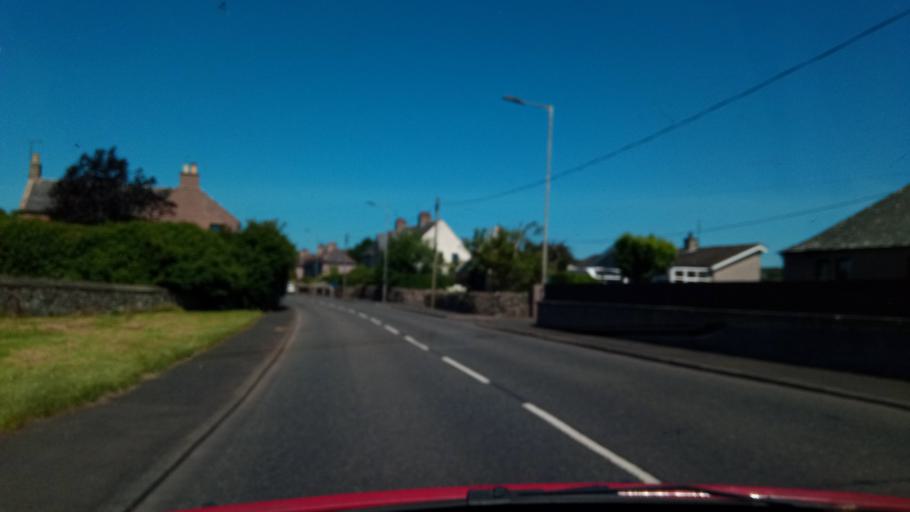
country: GB
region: Scotland
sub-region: The Scottish Borders
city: Kelso
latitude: 55.7032
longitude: -2.4638
